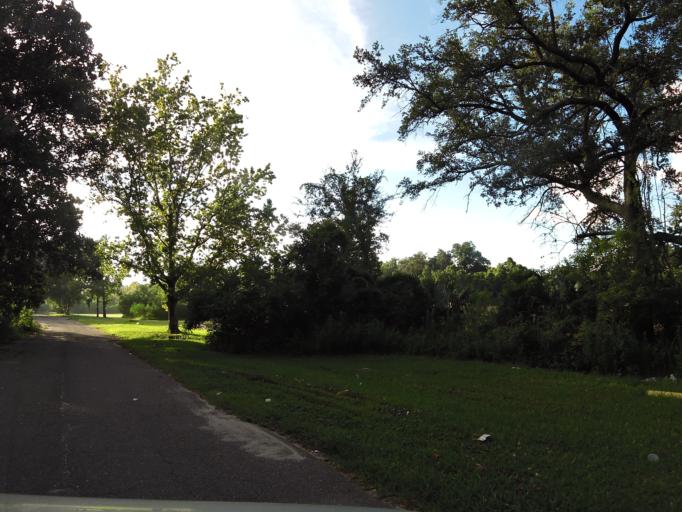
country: US
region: Florida
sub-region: Duval County
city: Jacksonville
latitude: 30.3799
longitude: -81.6683
